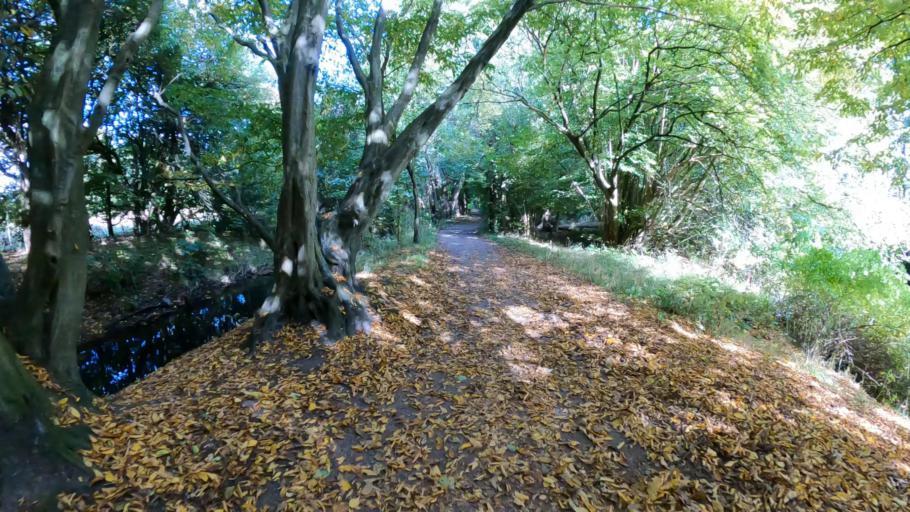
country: DE
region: Hamburg
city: Langenhorn
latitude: 53.6557
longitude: 9.9879
